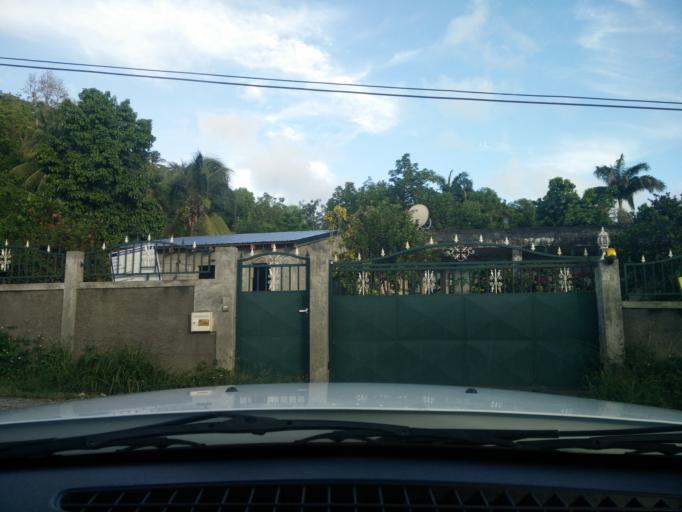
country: GP
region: Guadeloupe
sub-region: Guadeloupe
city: Les Abymes
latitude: 16.2512
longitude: -61.5099
